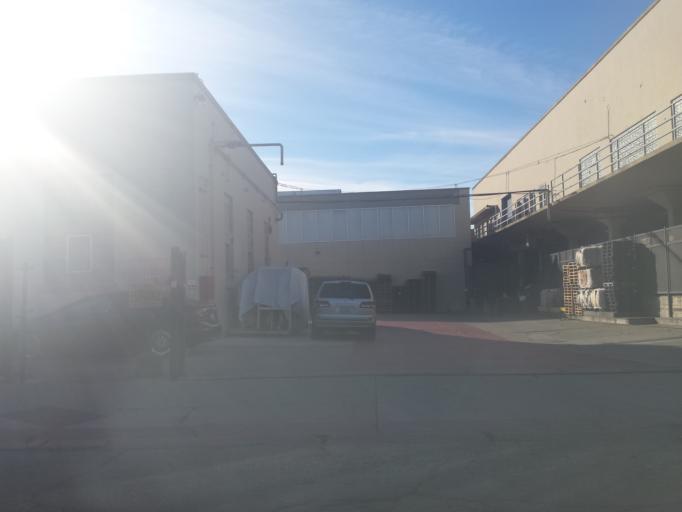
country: US
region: California
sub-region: Alameda County
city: Albany
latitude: 37.8657
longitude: -122.2993
